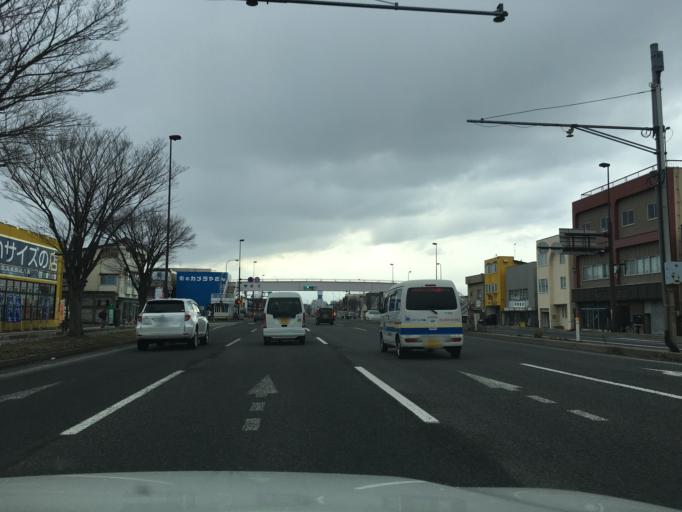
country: JP
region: Aomori
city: Aomori Shi
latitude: 40.8264
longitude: 140.7767
